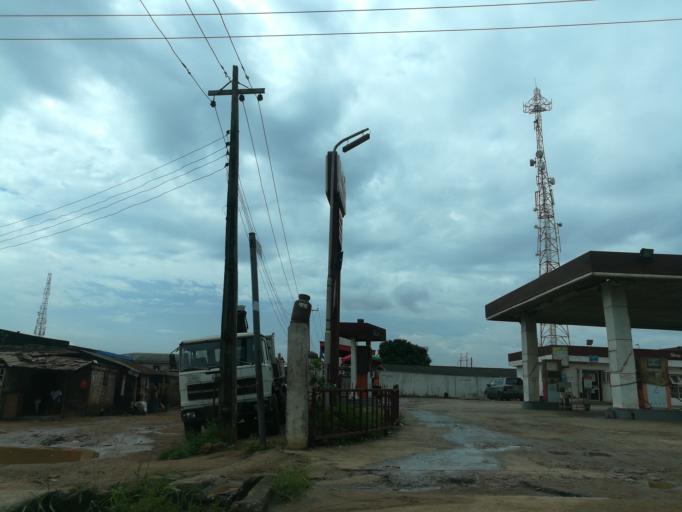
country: NG
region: Lagos
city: Ikorodu
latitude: 6.6307
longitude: 3.5084
